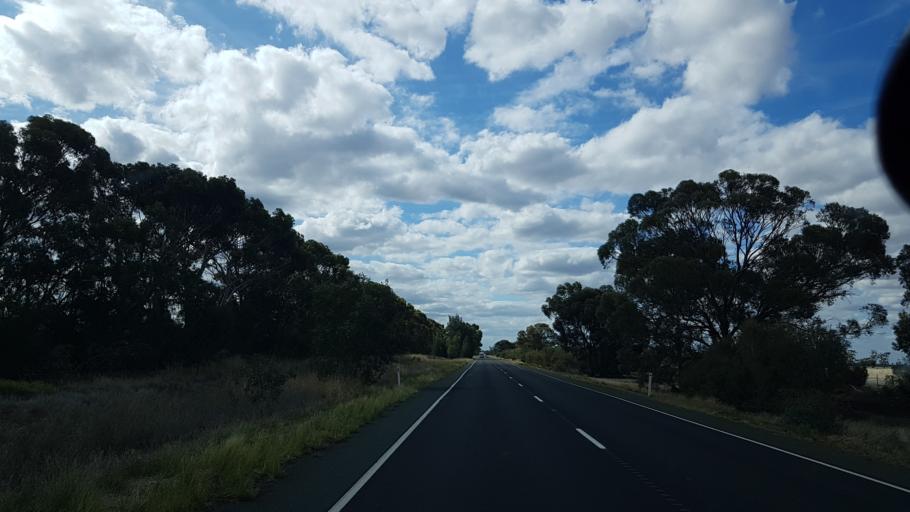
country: AU
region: Victoria
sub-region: Swan Hill
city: Swan Hill
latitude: -35.9804
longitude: 143.9449
